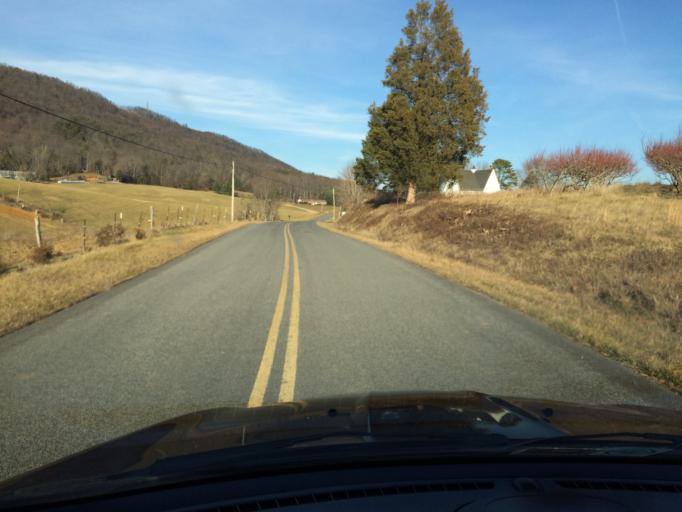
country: US
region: Virginia
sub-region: Botetourt County
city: Fincastle
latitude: 37.6164
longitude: -79.8378
